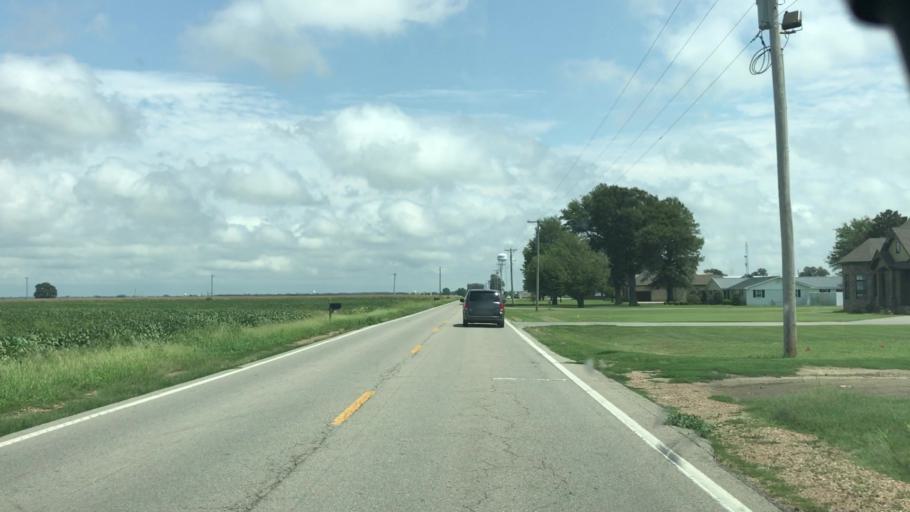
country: US
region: Missouri
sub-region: Pemiscot County
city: Hayti
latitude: 36.1760
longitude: -89.7268
